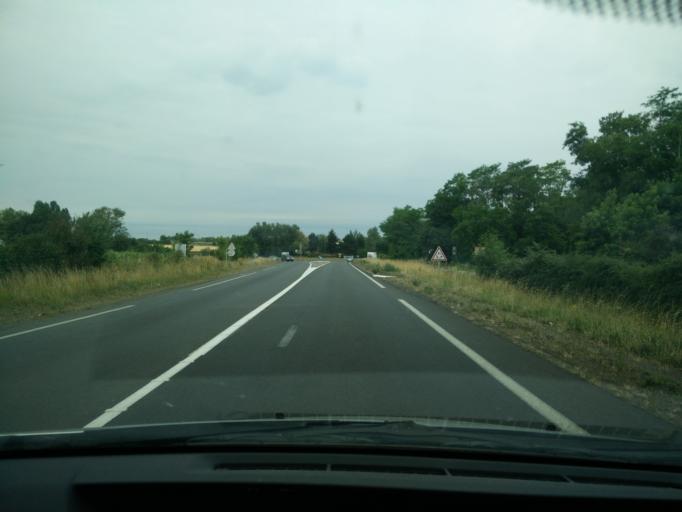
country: FR
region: Pays de la Loire
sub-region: Departement de Maine-et-Loire
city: Doue-la-Fontaine
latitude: 47.1878
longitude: -0.3009
